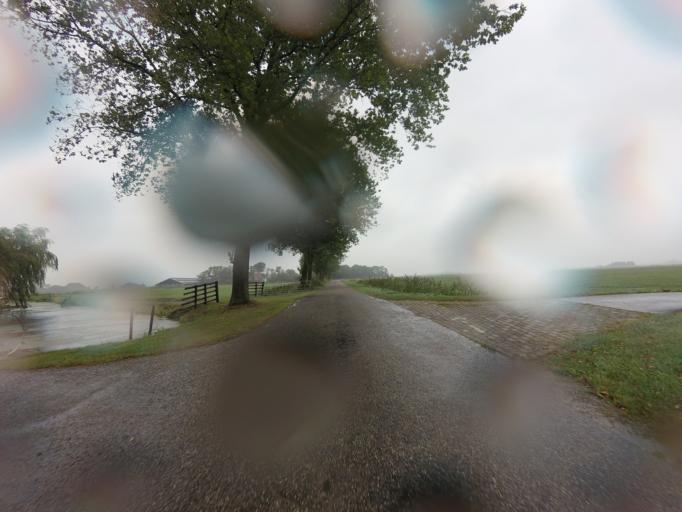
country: NL
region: Friesland
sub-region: Gemeente Boarnsterhim
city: Aldeboarn
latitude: 53.0716
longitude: 5.9288
